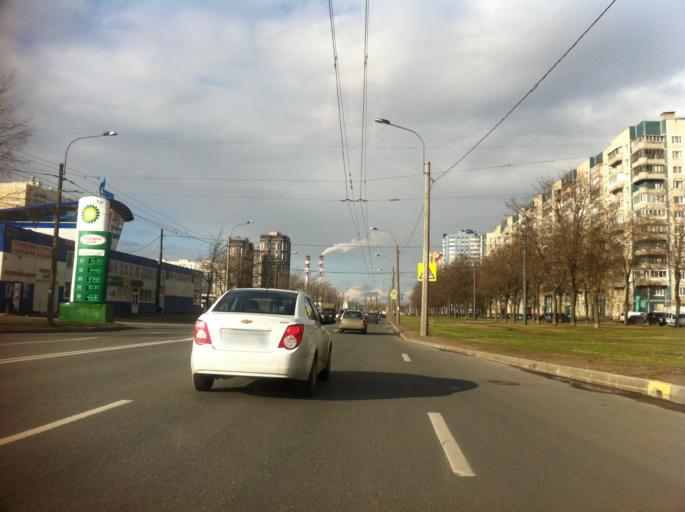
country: RU
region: St.-Petersburg
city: Uritsk
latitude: 59.8582
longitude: 30.1769
